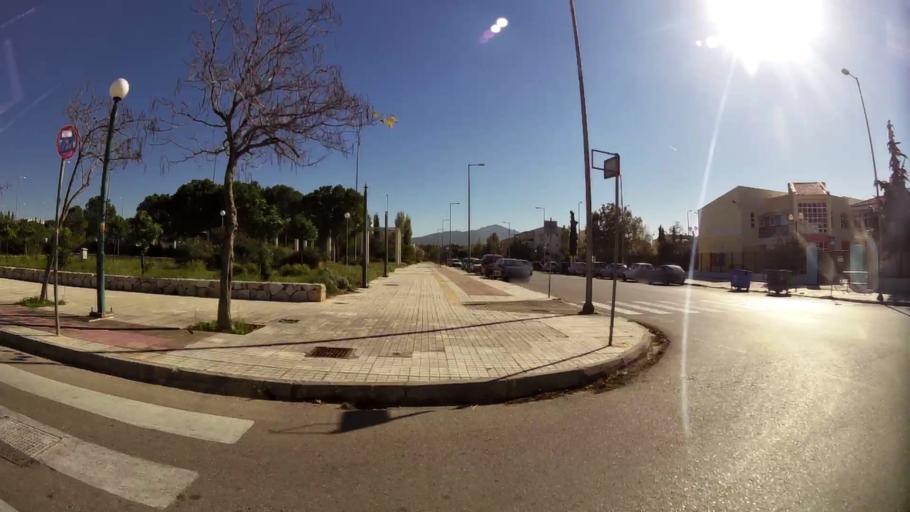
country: GR
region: Attica
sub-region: Nomarchia Anatolikis Attikis
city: Thrakomakedones
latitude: 38.1046
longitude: 23.7671
